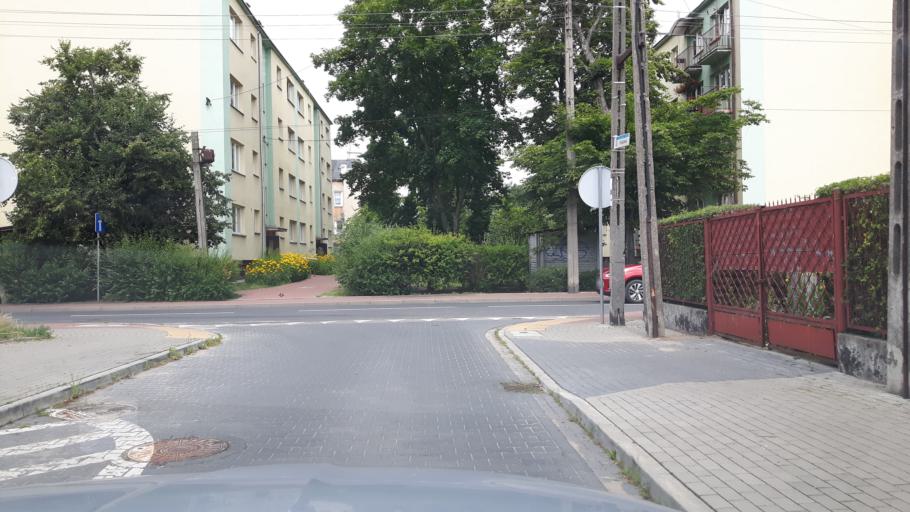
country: PL
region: Masovian Voivodeship
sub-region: Powiat wolominski
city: Wolomin
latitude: 52.3436
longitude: 21.2362
